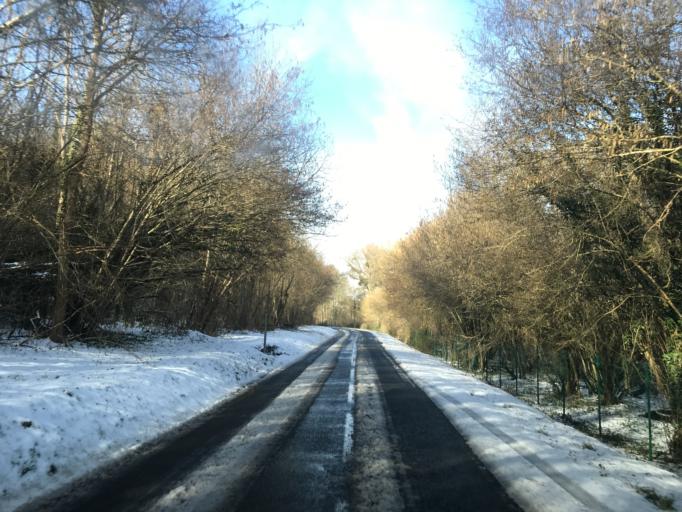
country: FR
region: Haute-Normandie
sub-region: Departement de l'Eure
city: Saint-Aubin-sur-Gaillon
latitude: 49.0781
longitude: 1.2815
